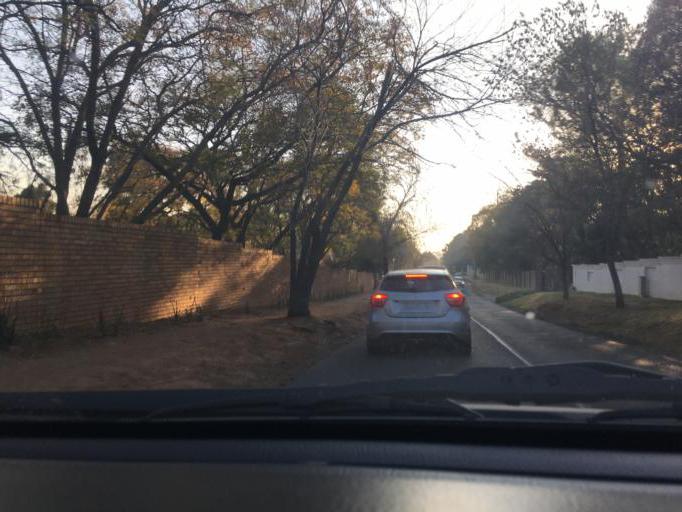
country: ZA
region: Gauteng
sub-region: City of Johannesburg Metropolitan Municipality
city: Diepsloot
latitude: -26.0704
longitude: 28.0003
